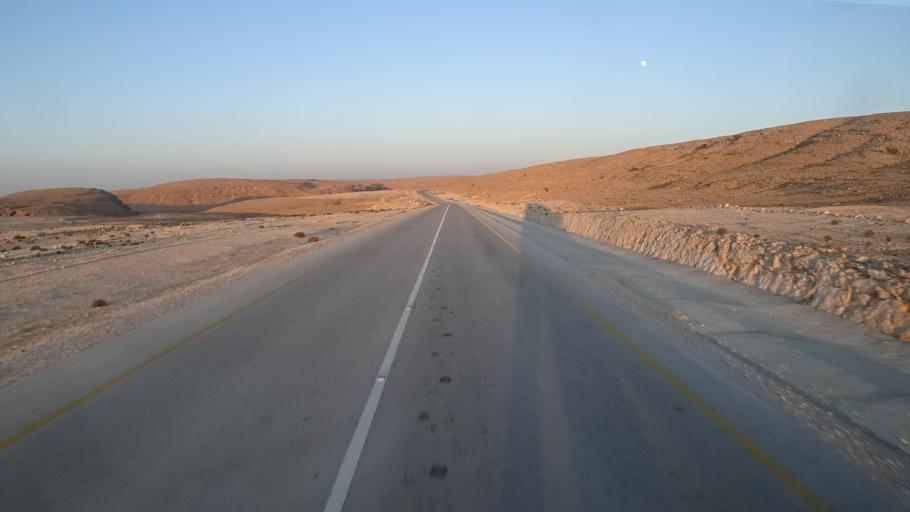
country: YE
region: Al Mahrah
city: Hawf
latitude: 16.9522
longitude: 53.3244
